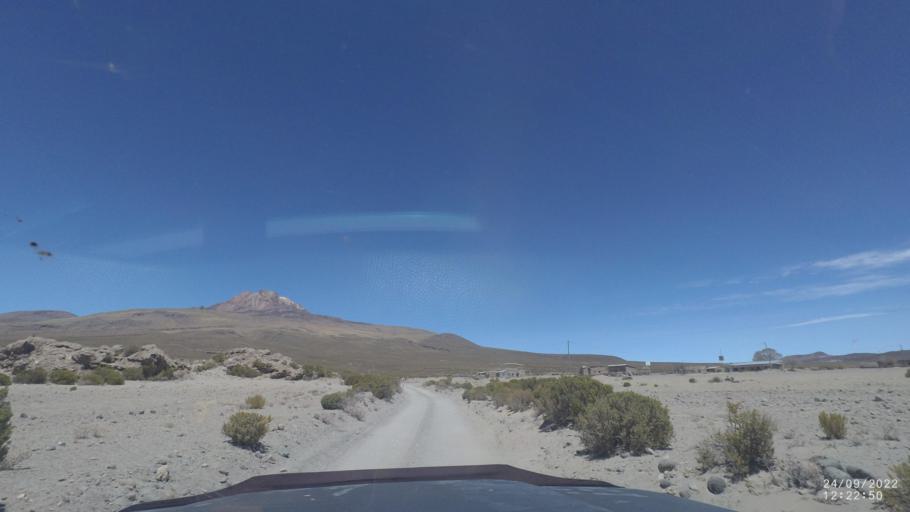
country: BO
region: Potosi
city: Colchani
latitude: -19.7593
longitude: -67.6645
